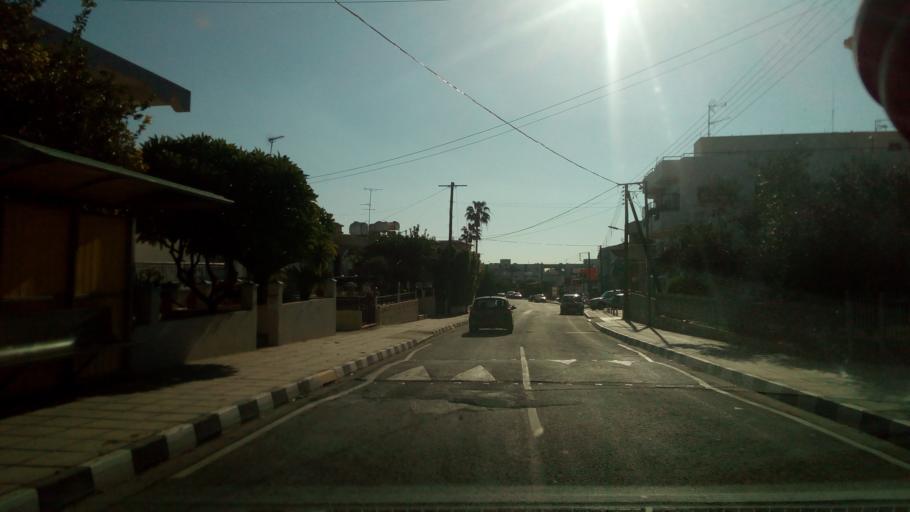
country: CY
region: Larnaka
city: Voroklini
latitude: 34.9850
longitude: 33.6537
